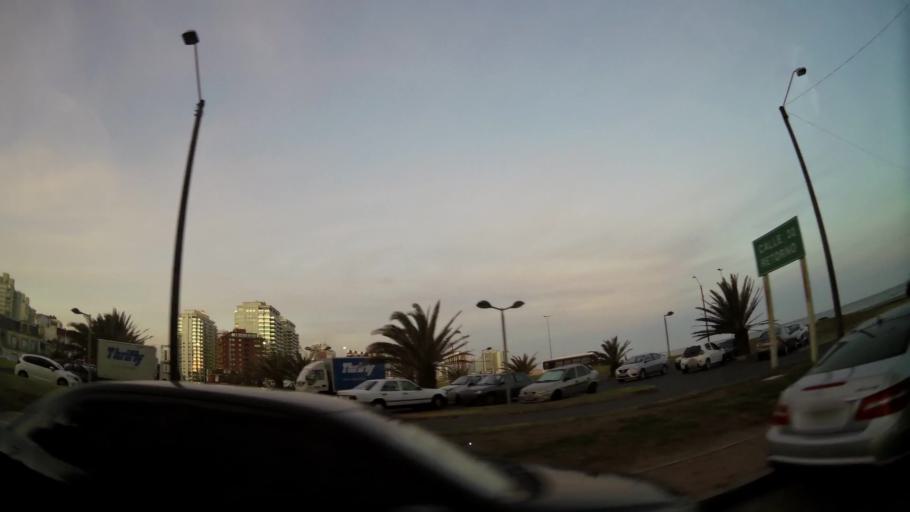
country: UY
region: Maldonado
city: Punta del Este
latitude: -34.9587
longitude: -54.9390
